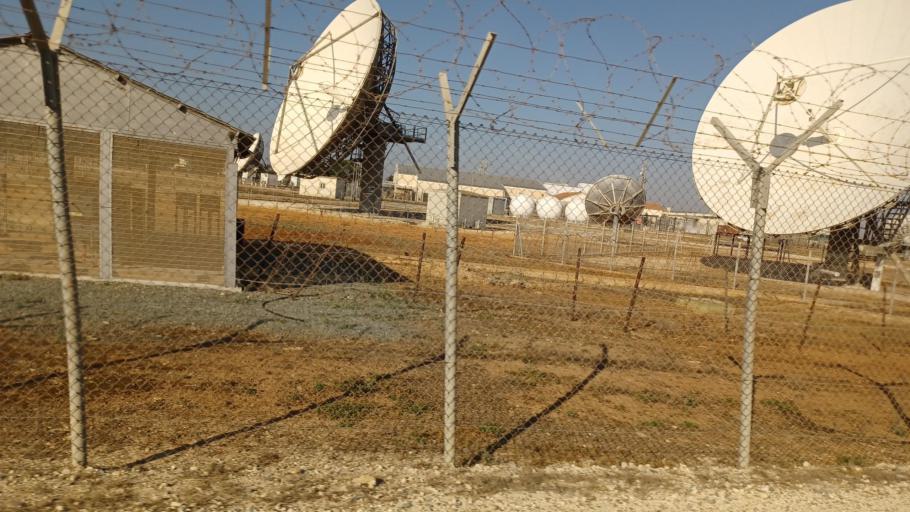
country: CY
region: Ammochostos
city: Acheritou
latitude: 35.0949
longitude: 33.8887
